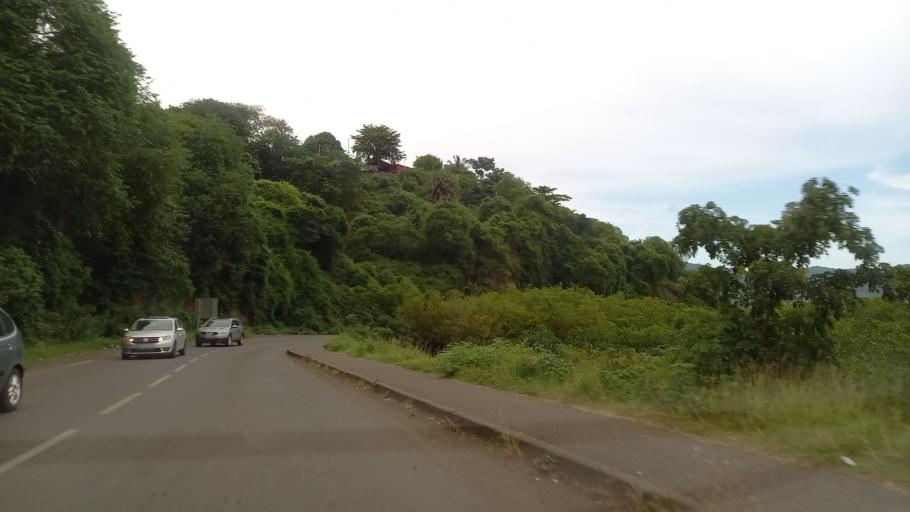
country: YT
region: Mamoudzou
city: Mamoudzou
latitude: -12.7755
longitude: 45.2315
